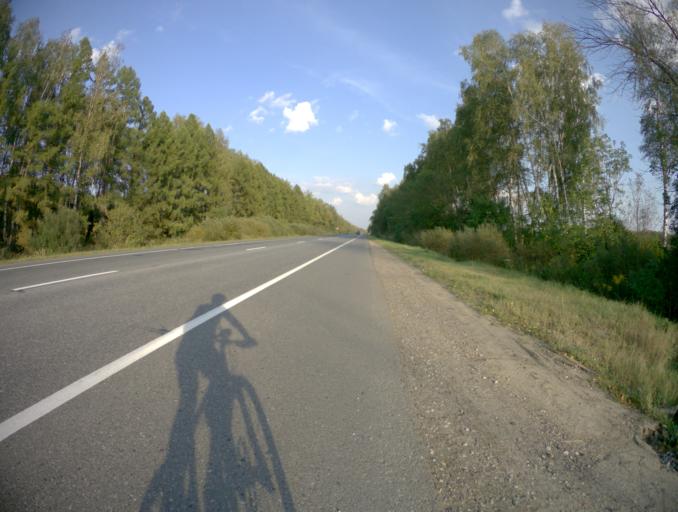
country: RU
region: Vladimir
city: Kameshkovo
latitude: 56.1972
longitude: 40.8633
